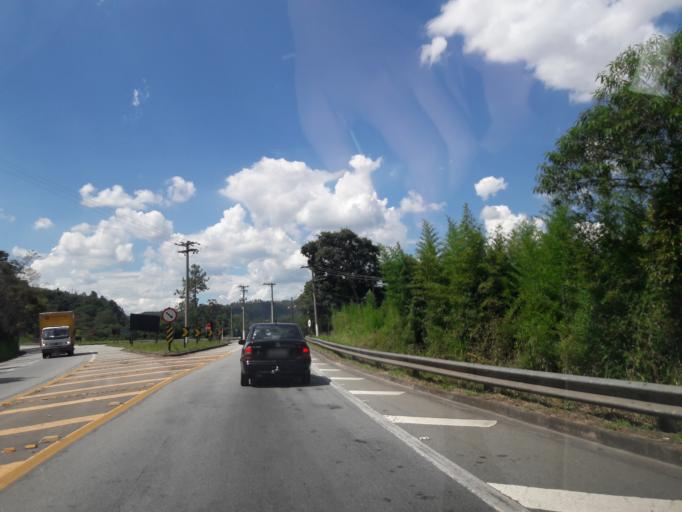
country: BR
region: Sao Paulo
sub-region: Francisco Morato
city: Francisco Morato
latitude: -23.2944
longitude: -46.8053
